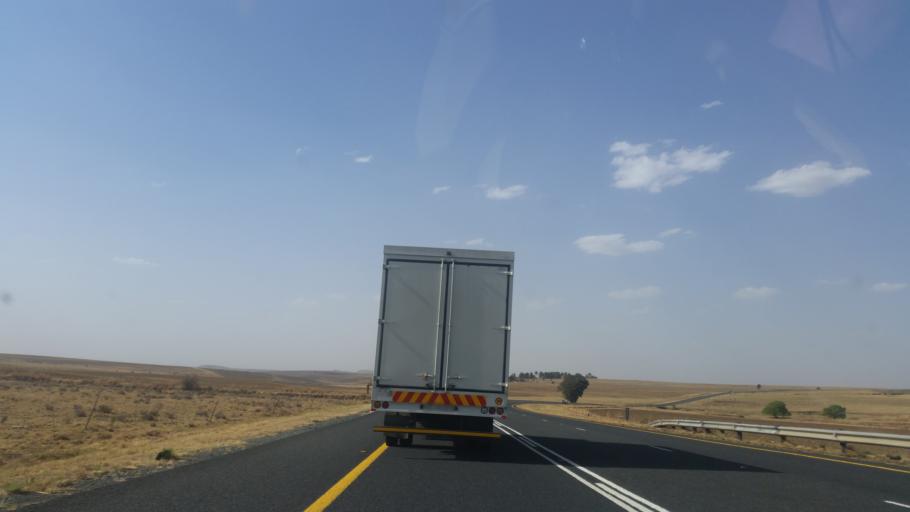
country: ZA
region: Orange Free State
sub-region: Thabo Mofutsanyana District Municipality
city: Bethlehem
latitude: -28.2928
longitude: 28.5969
